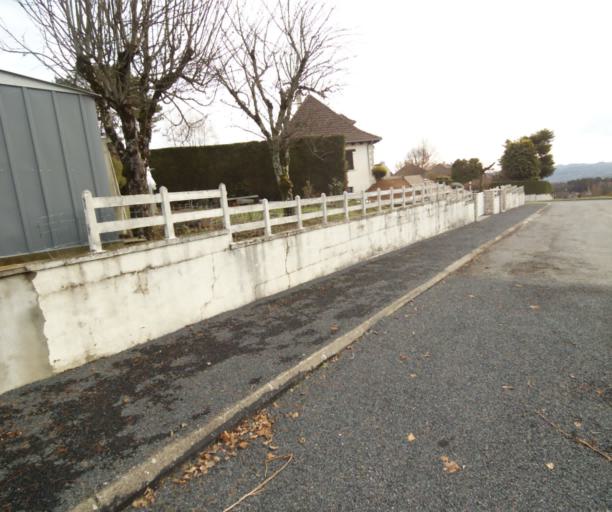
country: FR
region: Limousin
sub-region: Departement de la Correze
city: Chameyrat
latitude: 45.2599
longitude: 1.6998
